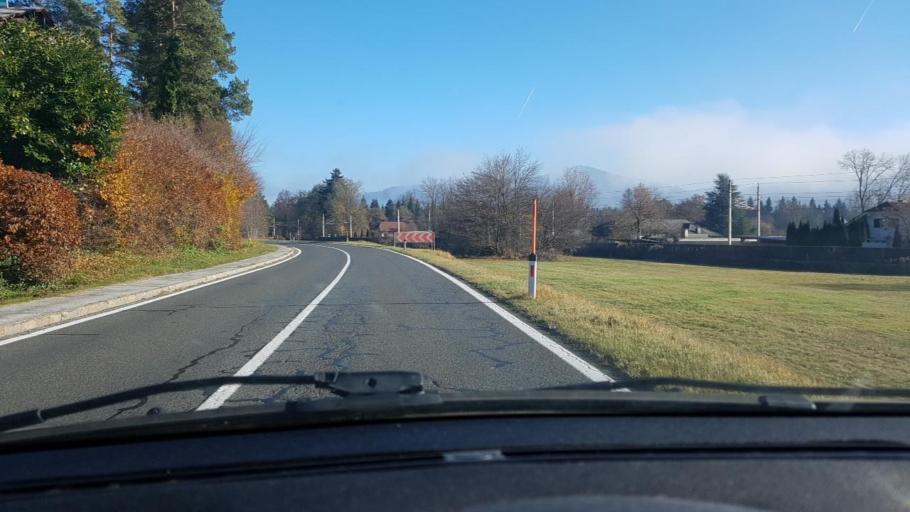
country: AT
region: Carinthia
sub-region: Politischer Bezirk Klagenfurt Land
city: Maria Worth
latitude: 46.6213
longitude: 14.1876
